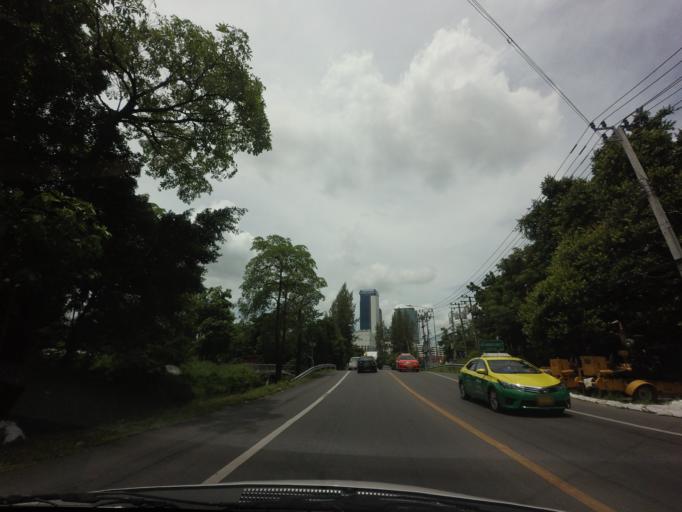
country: TH
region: Bangkok
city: Bang Na
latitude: 13.6710
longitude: 100.6445
